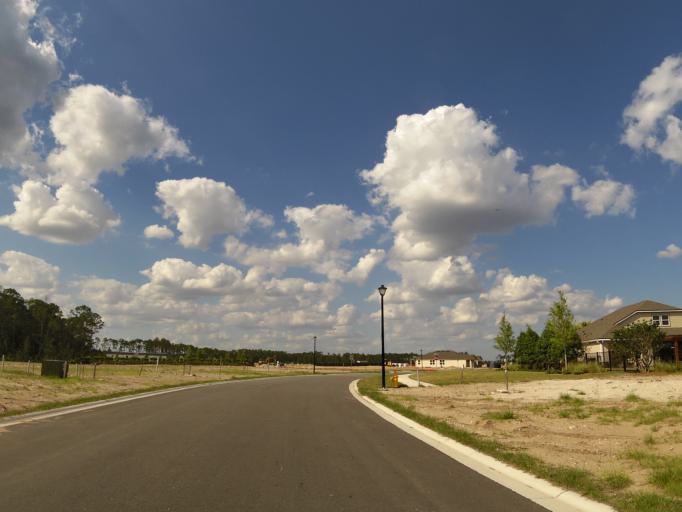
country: US
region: Florida
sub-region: Saint Johns County
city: Palm Valley
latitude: 30.1733
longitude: -81.5101
